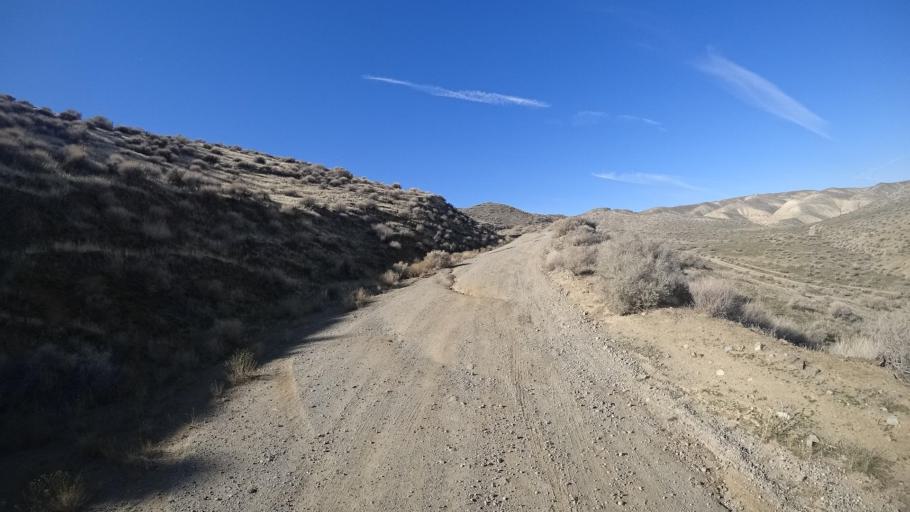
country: US
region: California
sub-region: Kern County
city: Maricopa
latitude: 35.0102
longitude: -119.4575
